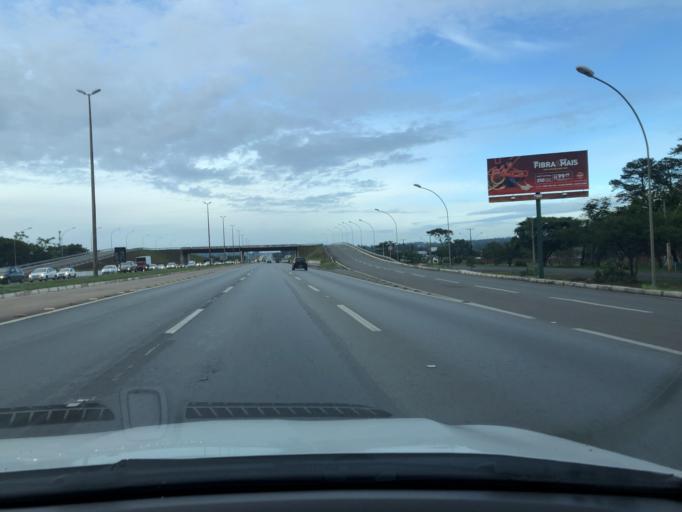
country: BR
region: Federal District
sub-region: Brasilia
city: Brasilia
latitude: -15.9254
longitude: -47.9772
